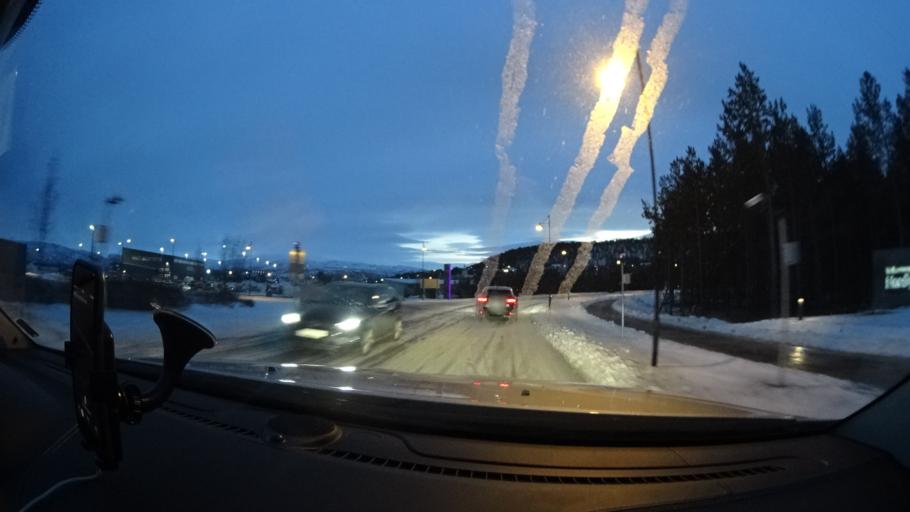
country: NO
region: Finnmark Fylke
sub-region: Alta
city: Alta
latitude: 69.9768
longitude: 23.3492
